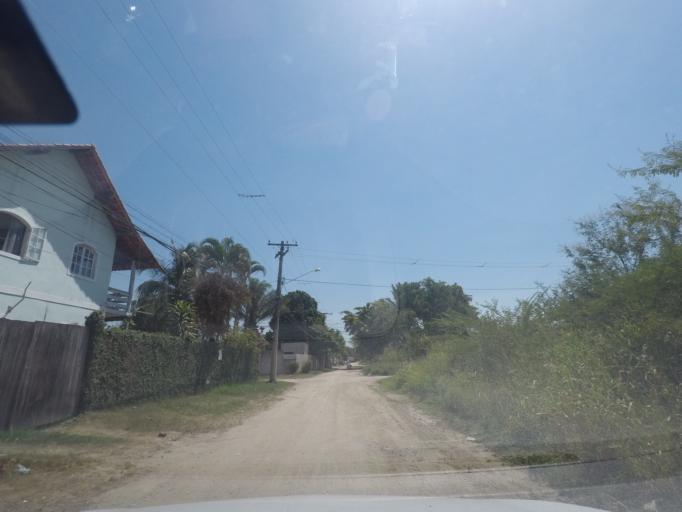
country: BR
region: Rio de Janeiro
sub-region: Niteroi
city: Niteroi
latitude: -22.9365
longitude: -43.0181
